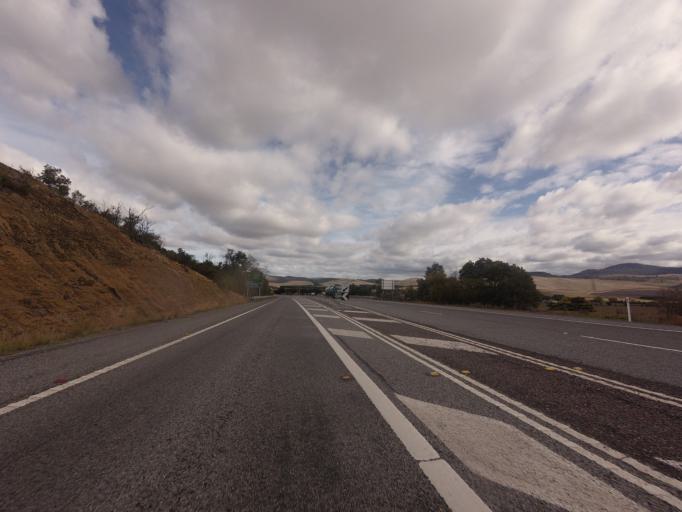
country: AU
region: Tasmania
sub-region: Brighton
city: Bridgewater
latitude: -42.4686
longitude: 147.1830
